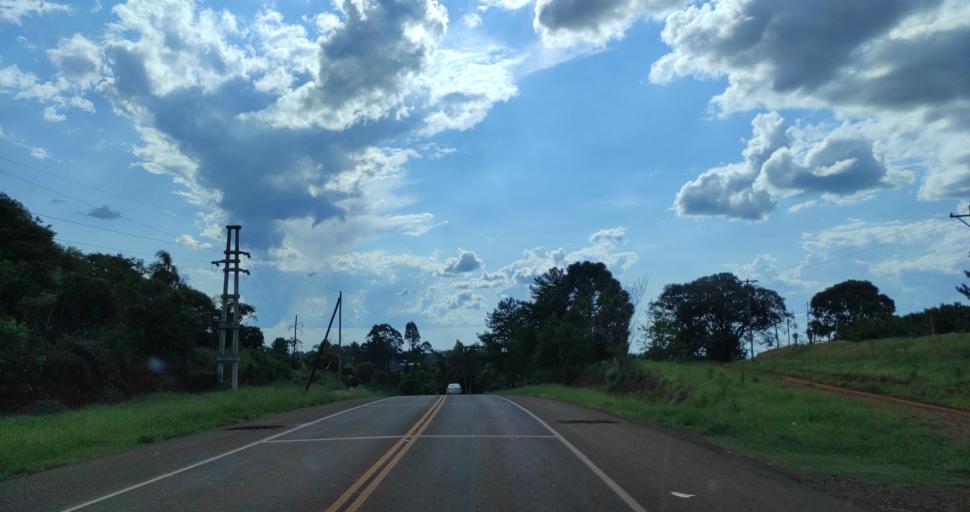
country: AR
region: Misiones
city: Bernardo de Irigoyen
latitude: -26.2928
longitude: -53.7672
